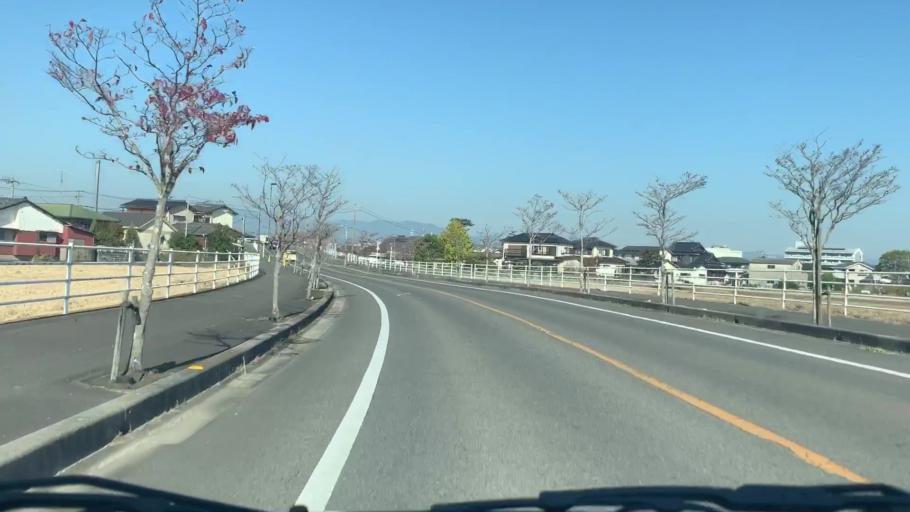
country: JP
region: Saga Prefecture
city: Saga-shi
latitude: 33.2350
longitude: 130.3124
